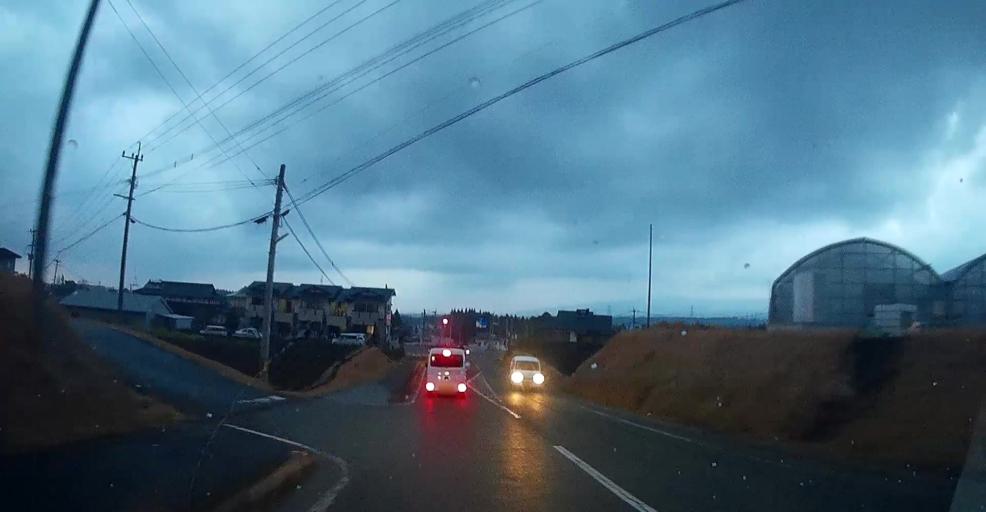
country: JP
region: Kumamoto
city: Ozu
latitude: 32.8389
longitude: 130.9164
